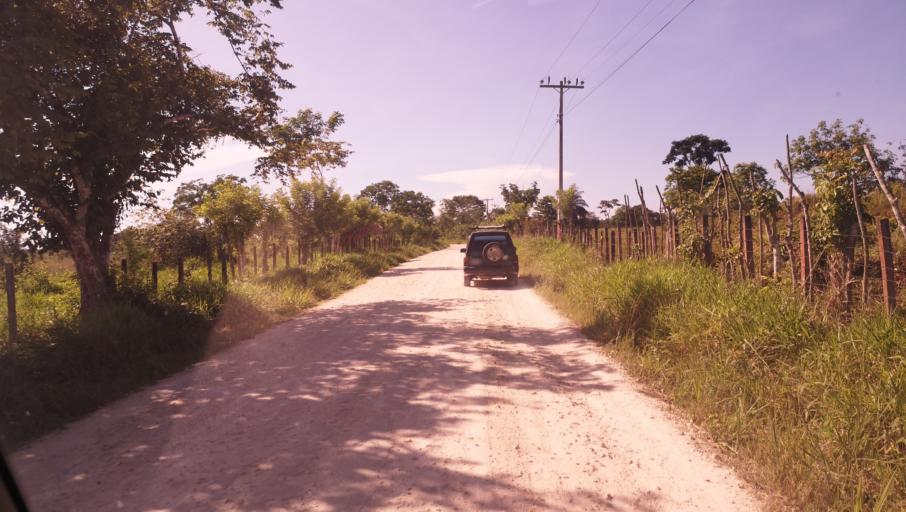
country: GT
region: Peten
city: Dolores
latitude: 16.7162
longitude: -89.3685
